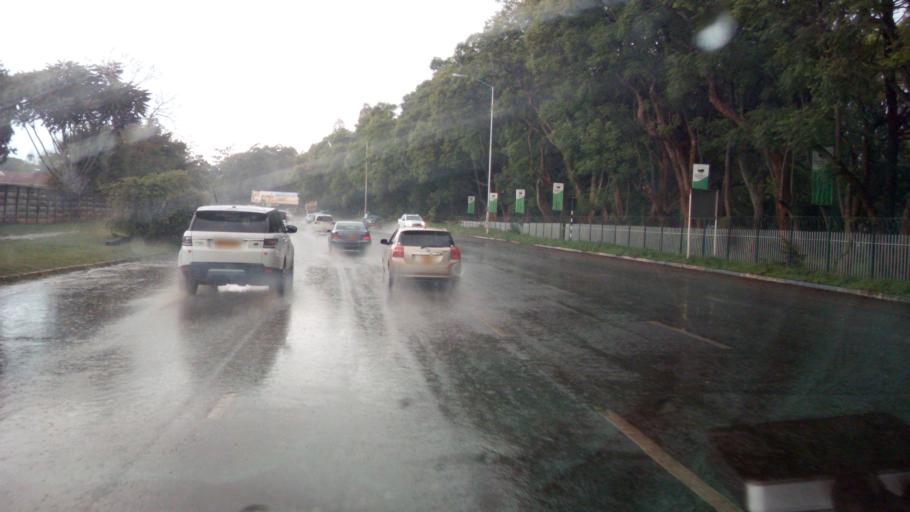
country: ZW
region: Harare
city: Harare
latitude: -17.8066
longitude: 31.0587
